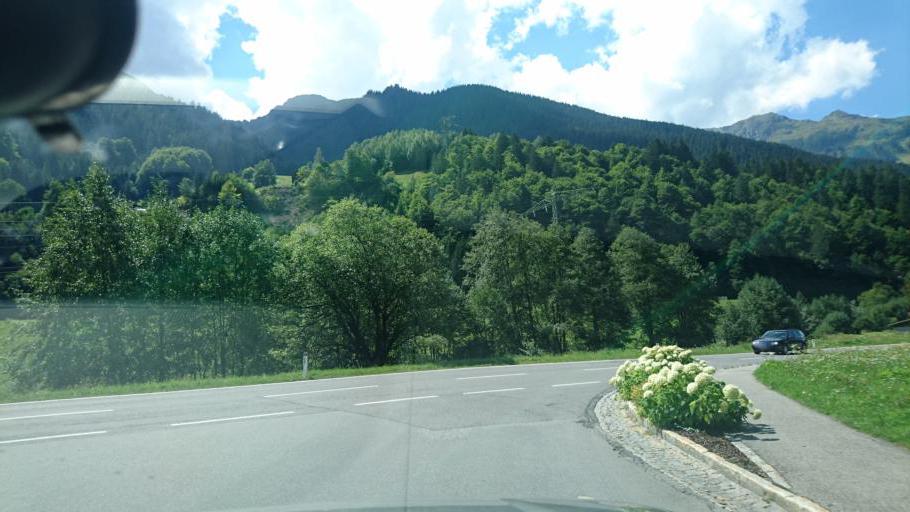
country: AT
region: Vorarlberg
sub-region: Politischer Bezirk Bludenz
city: Gaschurn
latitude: 46.9705
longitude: 10.0539
